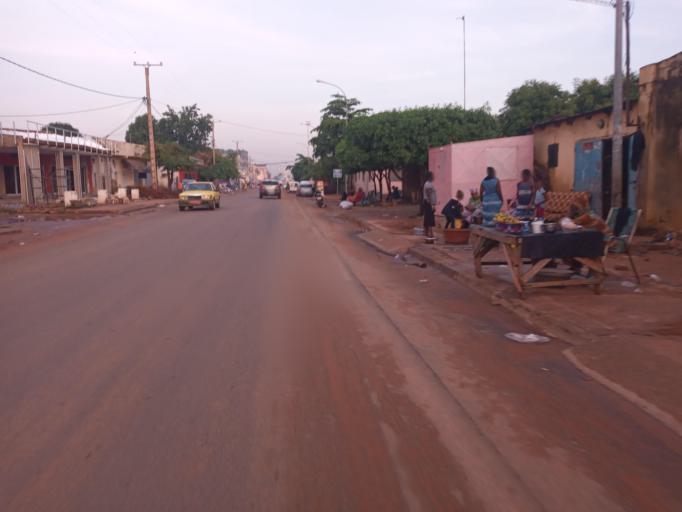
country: ML
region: Bamako
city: Bamako
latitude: 12.6283
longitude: -8.0373
